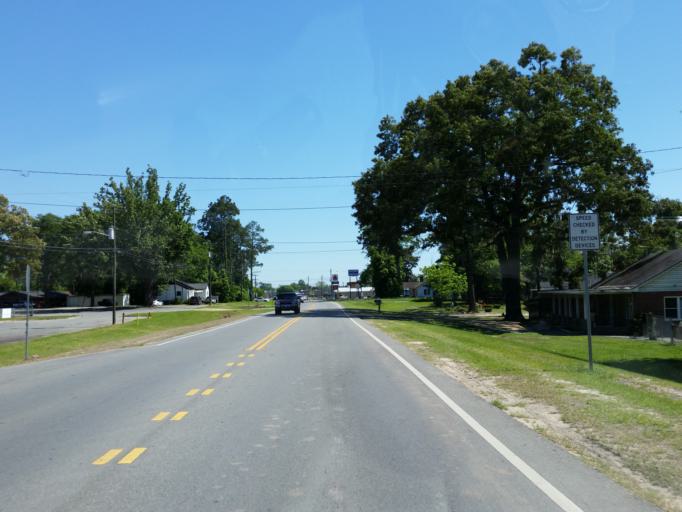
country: US
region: Georgia
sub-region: Cook County
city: Adel
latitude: 31.1499
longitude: -83.4278
